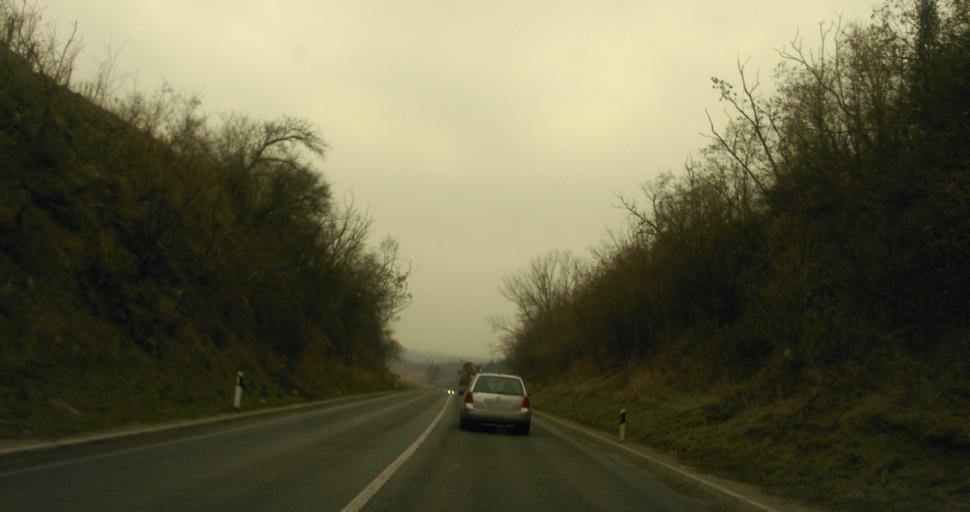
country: RS
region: Central Serbia
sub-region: Belgrade
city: Zvezdara
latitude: 44.7315
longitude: 20.5382
